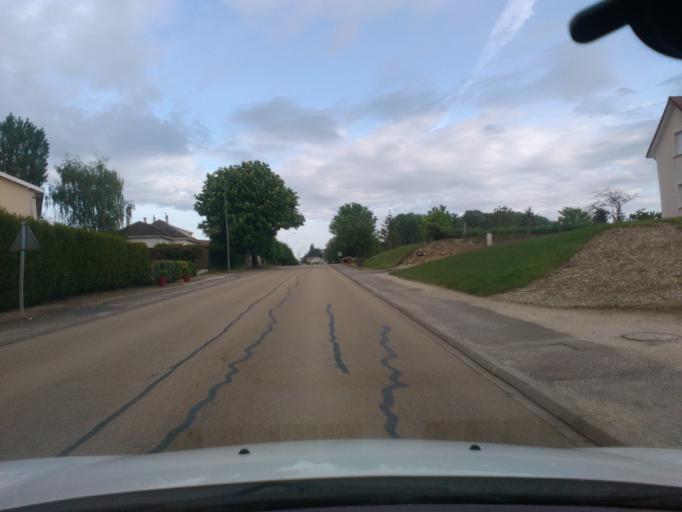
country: FR
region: Champagne-Ardenne
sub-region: Departement de la Haute-Marne
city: Lavilleneuve-au-Roi
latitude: 48.2231
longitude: 4.8931
